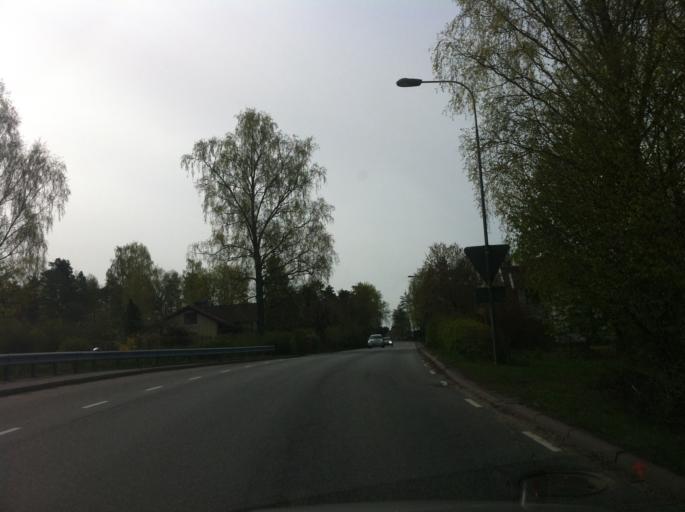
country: SE
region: Vaestra Goetaland
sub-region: Marks Kommun
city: Kinna
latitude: 57.4783
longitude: 12.7044
